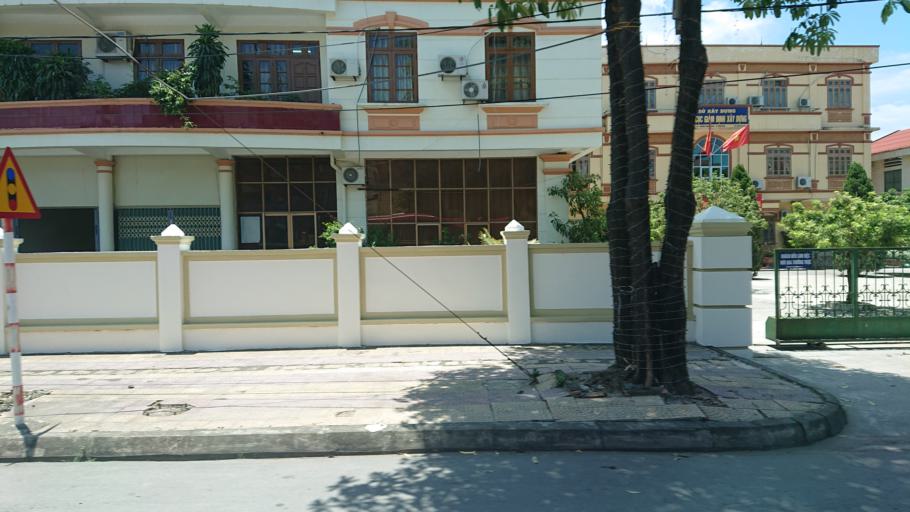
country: VN
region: Ninh Binh
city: Thanh Pho Ninh Binh
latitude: 20.2657
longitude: 105.9685
